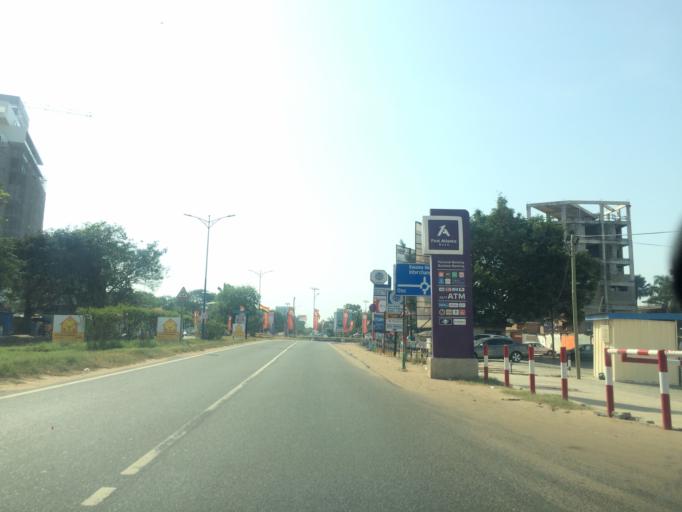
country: GH
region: Greater Accra
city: Accra
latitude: 5.5663
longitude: -0.1797
